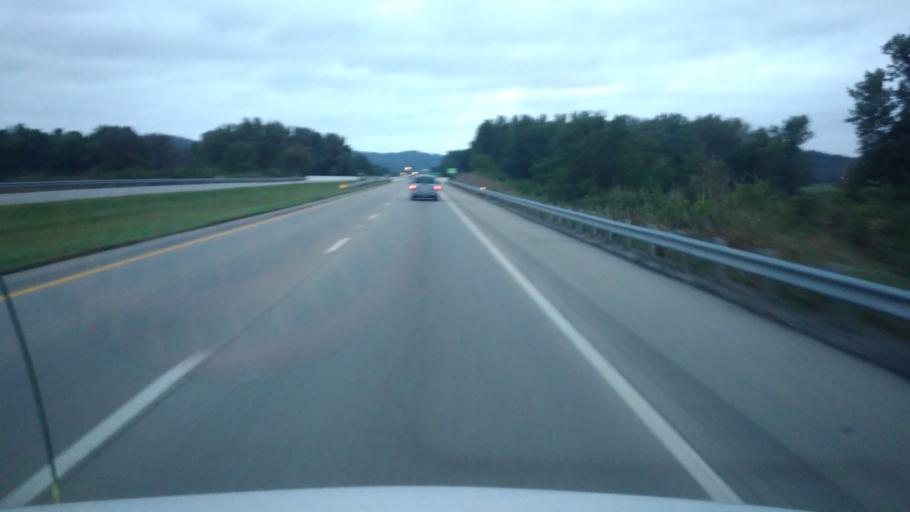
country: US
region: Ohio
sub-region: Ross County
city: Chillicothe
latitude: 39.3029
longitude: -82.9422
